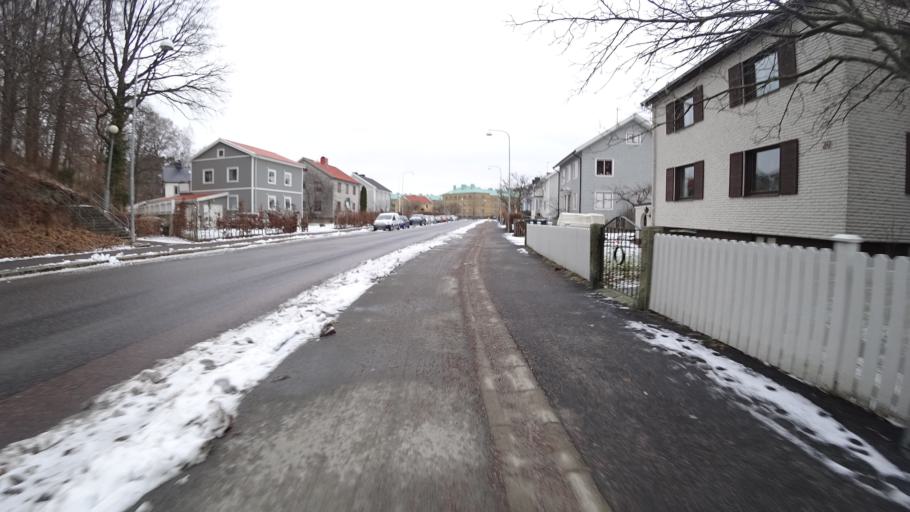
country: SE
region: Vaestra Goetaland
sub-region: Goteborg
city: Majorna
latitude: 57.6783
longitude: 11.9283
